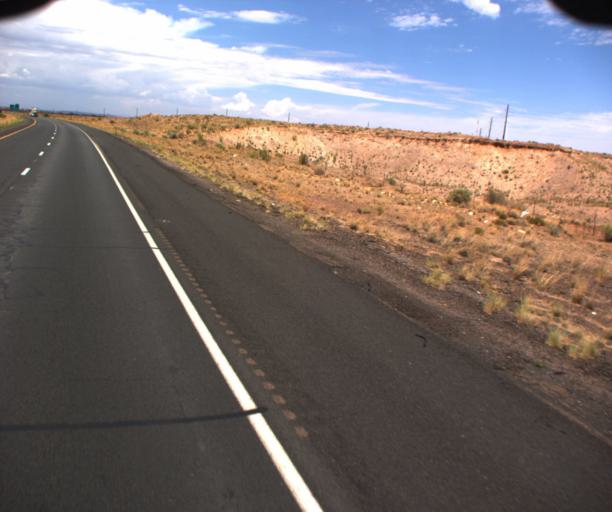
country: US
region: Arizona
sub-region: Navajo County
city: Winslow
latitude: 35.0057
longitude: -110.6145
